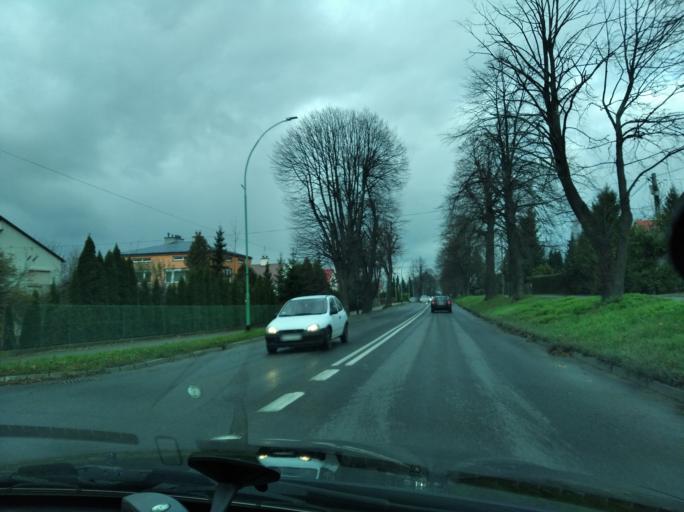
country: PL
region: Subcarpathian Voivodeship
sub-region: Powiat lancucki
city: Lancut
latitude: 50.0736
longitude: 22.2368
